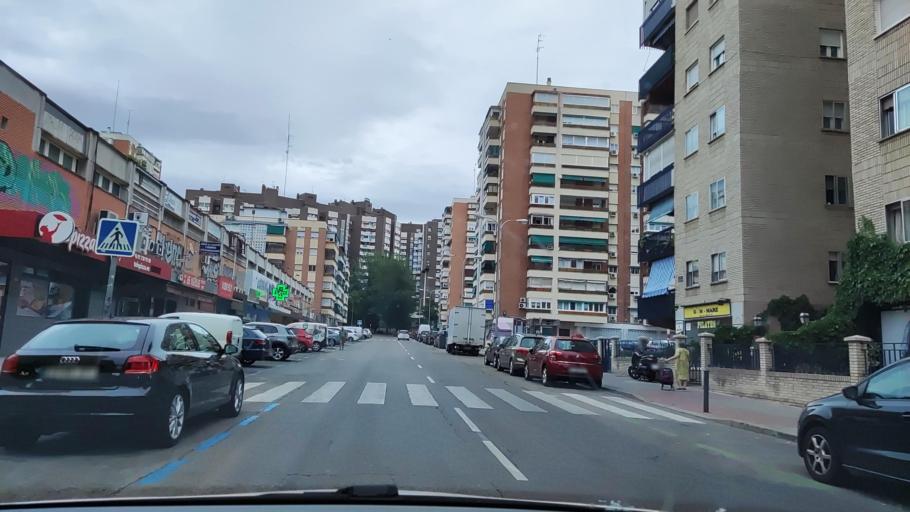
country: ES
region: Madrid
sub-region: Provincia de Madrid
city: Tetuan de las Victorias
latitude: 40.4851
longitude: -3.7004
